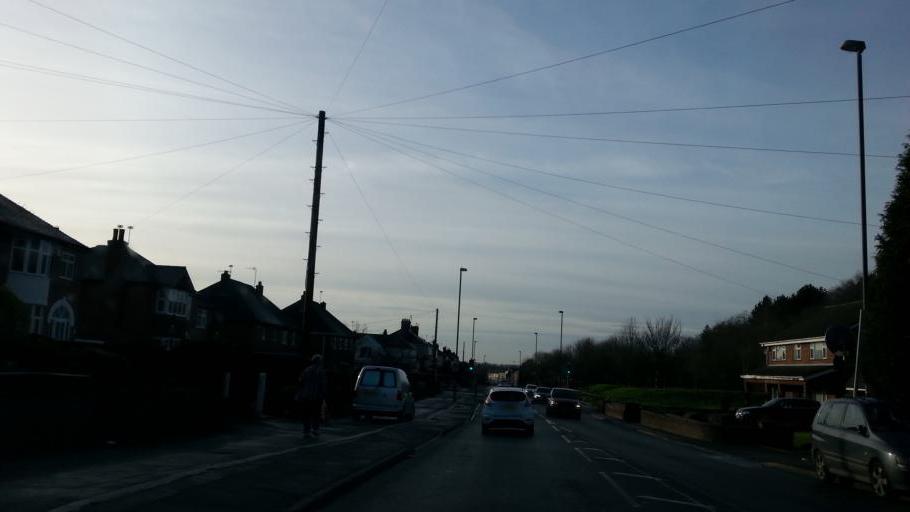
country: GB
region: England
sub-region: Stoke-on-Trent
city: Stoke-on-Trent
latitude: 53.0427
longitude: -2.1746
